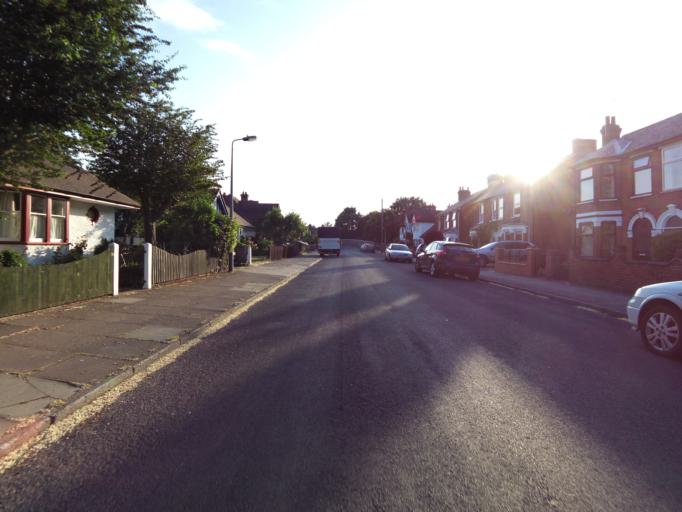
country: GB
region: England
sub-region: Suffolk
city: Ipswich
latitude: 52.0560
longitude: 1.1787
